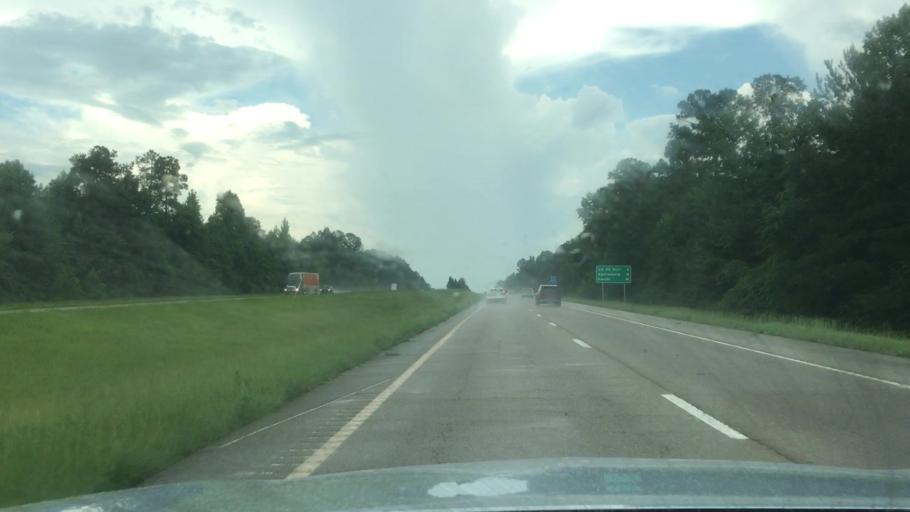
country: US
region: Mississippi
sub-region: Lamar County
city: Purvis
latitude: 31.1511
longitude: -89.3622
